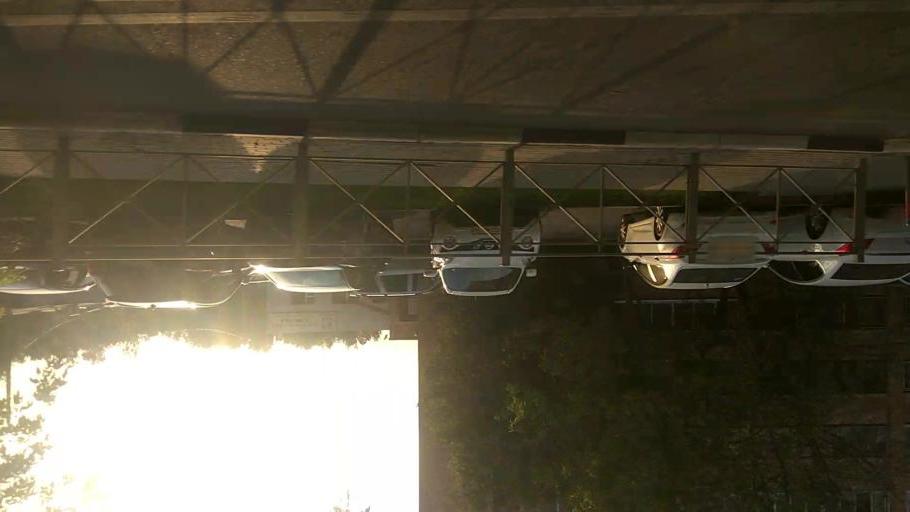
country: RU
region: Moskovskaya
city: Korolev
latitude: 55.9238
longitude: 37.7833
